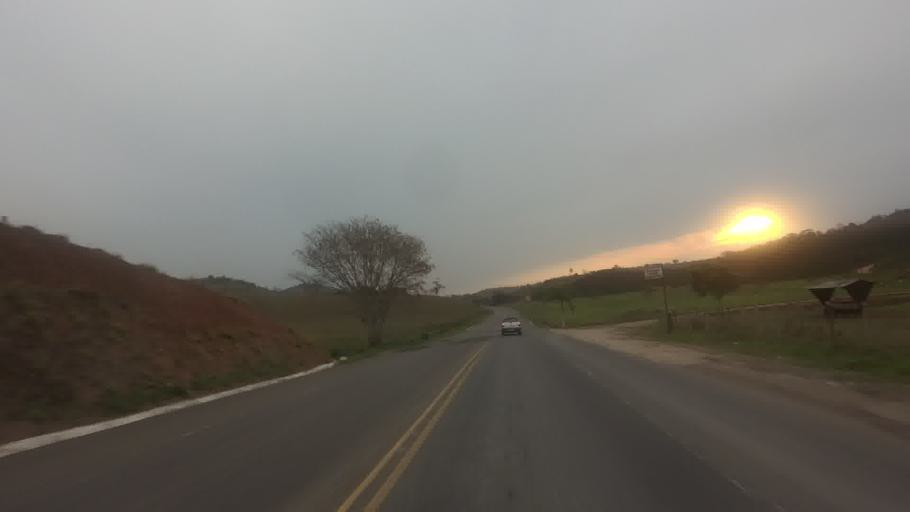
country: BR
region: Minas Gerais
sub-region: Recreio
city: Recreio
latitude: -21.6596
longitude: -42.3733
